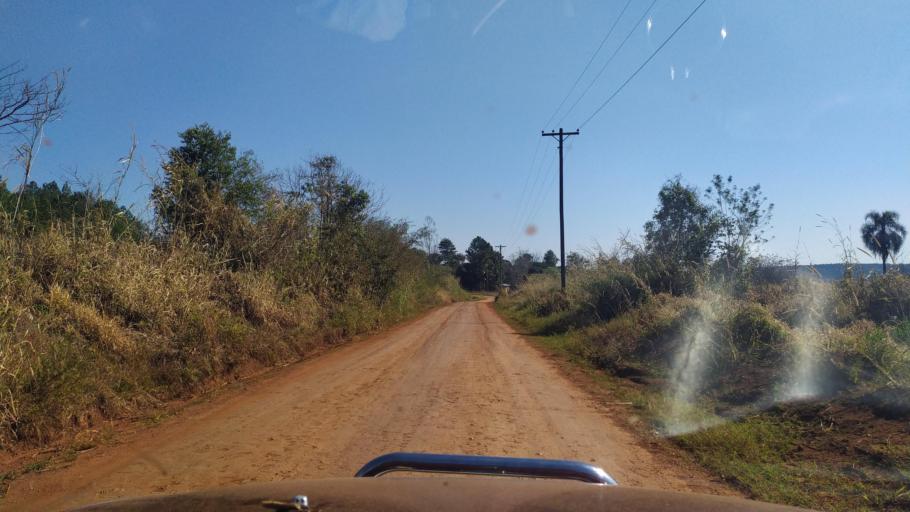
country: AR
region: Misiones
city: El Alcazar
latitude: -26.7153
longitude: -54.7149
